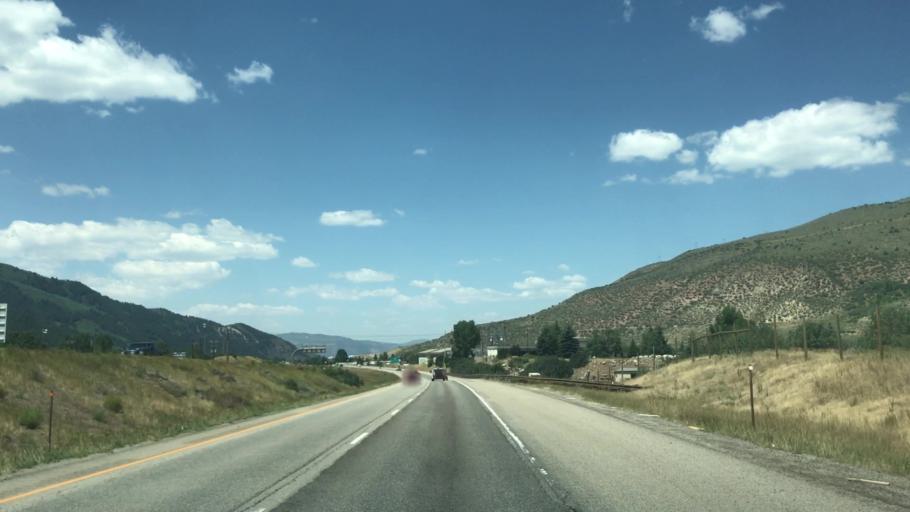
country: US
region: Colorado
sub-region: Eagle County
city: Minturn
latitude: 39.6195
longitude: -106.4682
